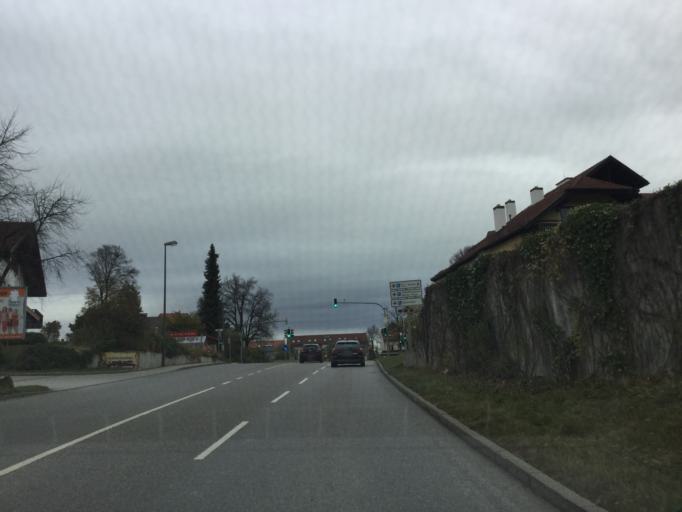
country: DE
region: Bavaria
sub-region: Upper Bavaria
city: Murnau am Staffelsee
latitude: 47.6798
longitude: 11.1967
